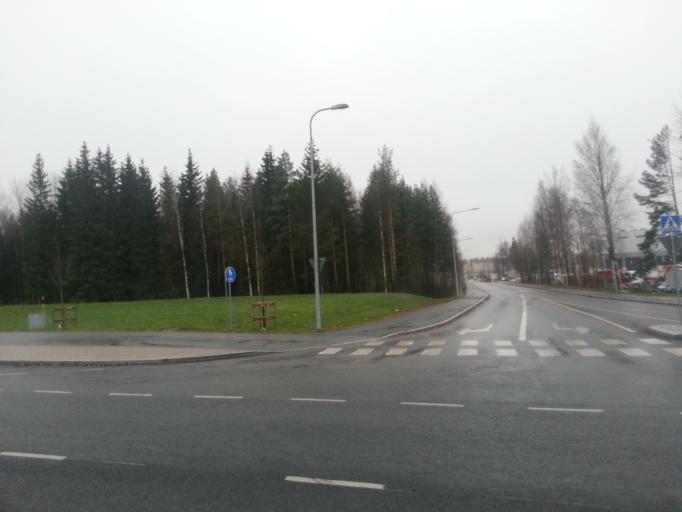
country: FI
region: Uusimaa
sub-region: Helsinki
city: Vantaa
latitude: 60.3023
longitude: 24.9516
